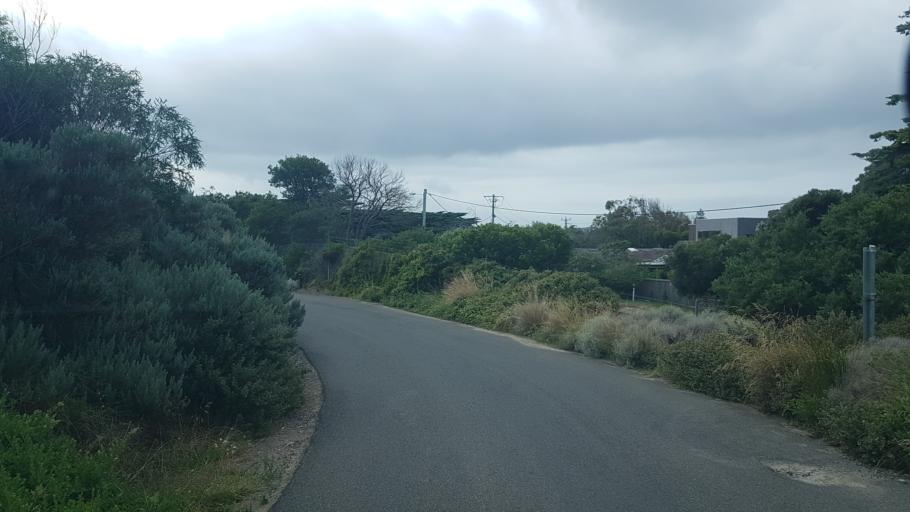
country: AU
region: Victoria
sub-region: Mornington Peninsula
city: Sorrento
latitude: -38.3264
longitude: 144.7044
